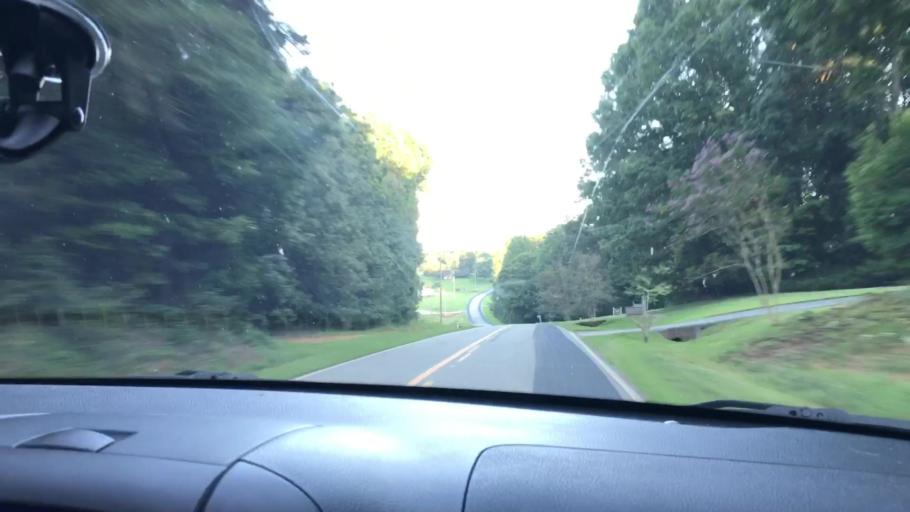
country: US
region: North Carolina
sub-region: Randolph County
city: Ramseur
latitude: 35.7832
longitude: -79.6395
